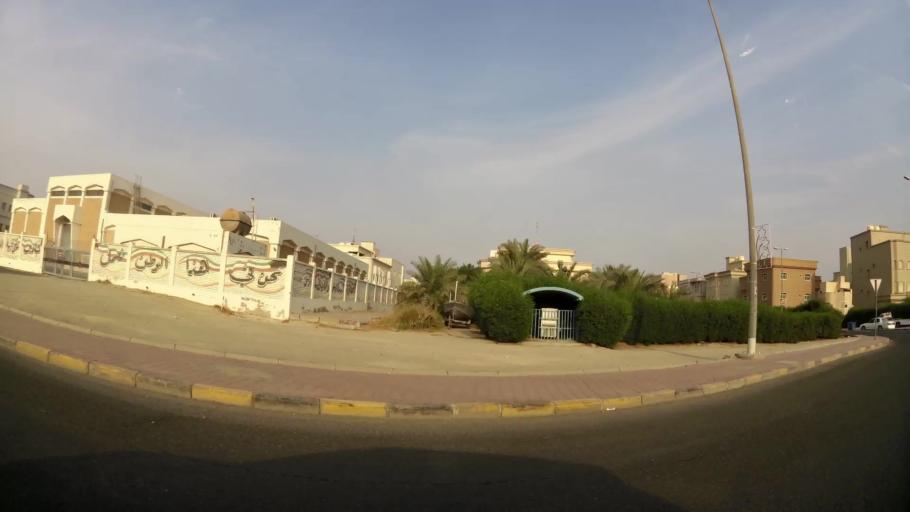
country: KW
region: Mubarak al Kabir
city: Mubarak al Kabir
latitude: 29.1846
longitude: 48.0810
